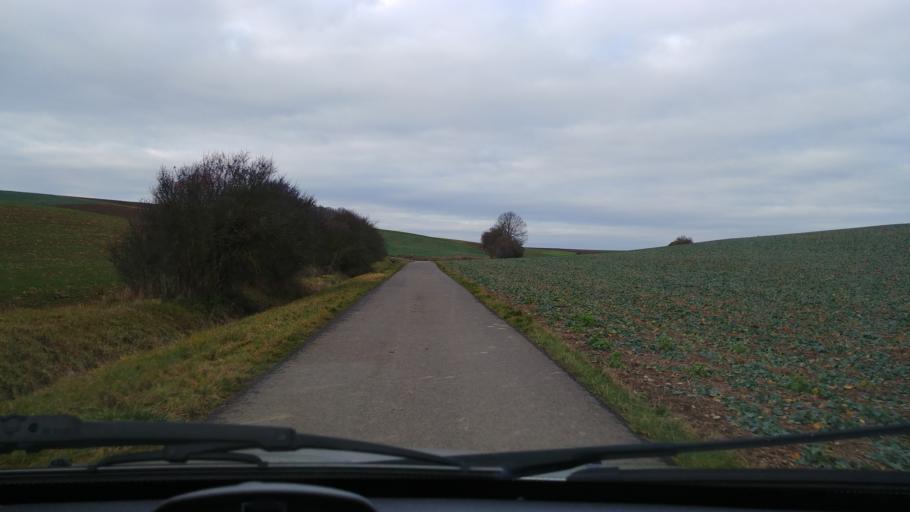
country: DE
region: Bavaria
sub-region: Regierungsbezirk Unterfranken
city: Arnstein
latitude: 50.0085
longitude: 9.9907
